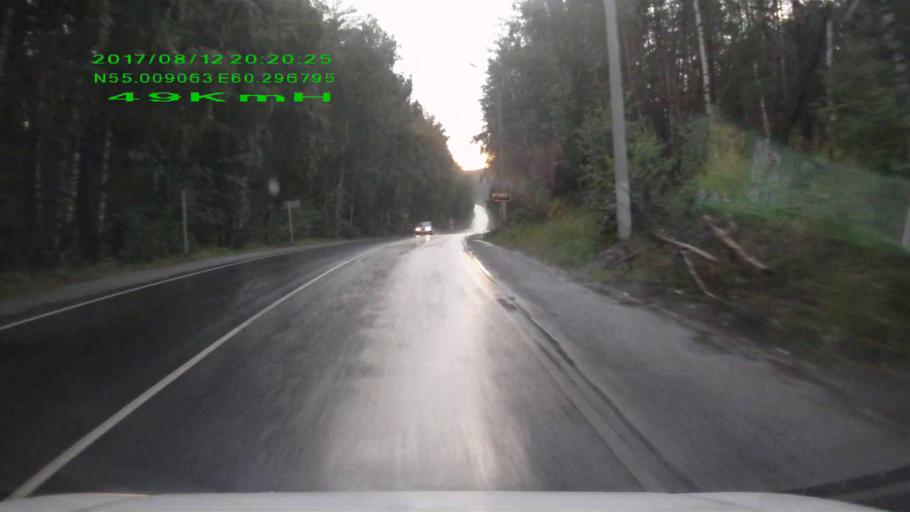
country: RU
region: Chelyabinsk
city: Chebarkul'
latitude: 55.0091
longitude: 60.2965
